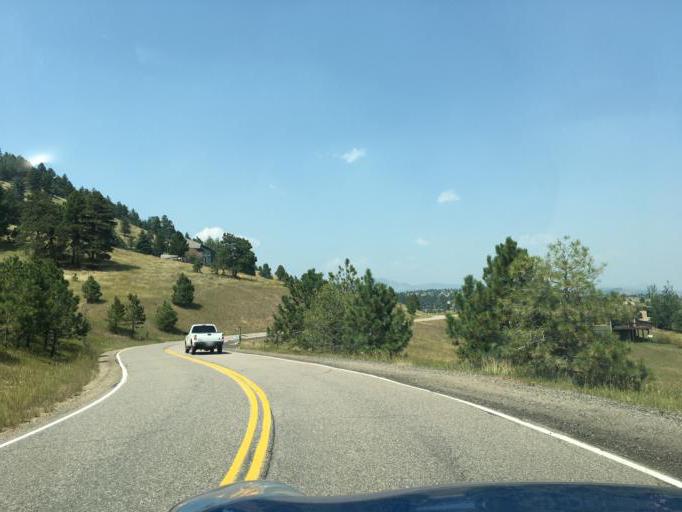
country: US
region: Colorado
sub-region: Jefferson County
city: Genesee
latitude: 39.6981
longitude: -105.2713
